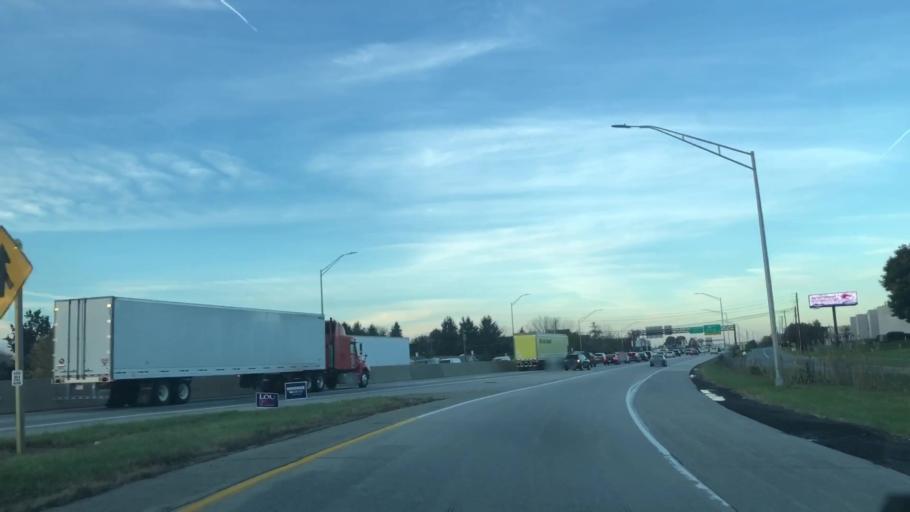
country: US
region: Pennsylvania
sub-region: Lehigh County
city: Fountain Hill
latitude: 40.6471
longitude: -75.4206
